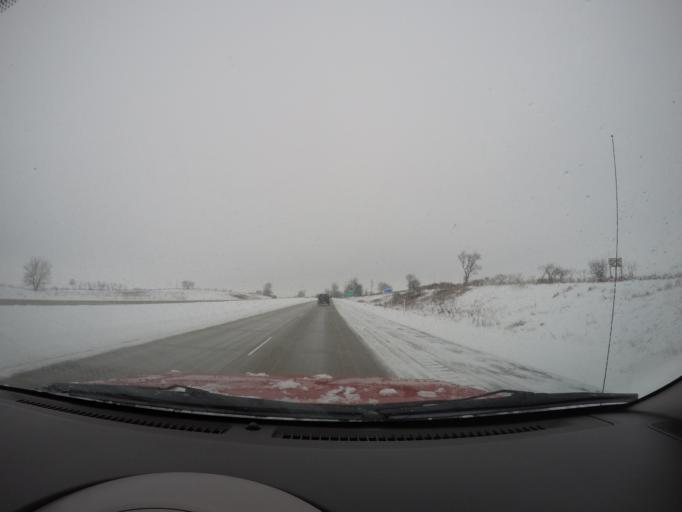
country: US
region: Minnesota
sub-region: Winona County
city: Saint Charles
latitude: 43.9444
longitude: -92.0363
